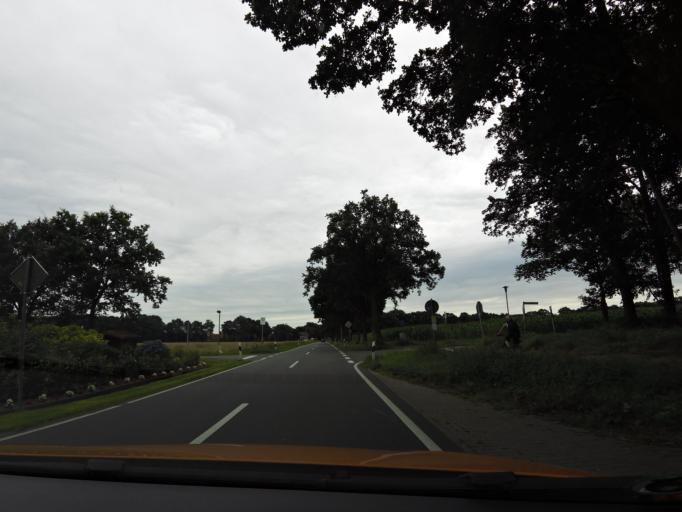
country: DE
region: Lower Saxony
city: Wiefelstede
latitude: 53.1902
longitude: 8.1485
